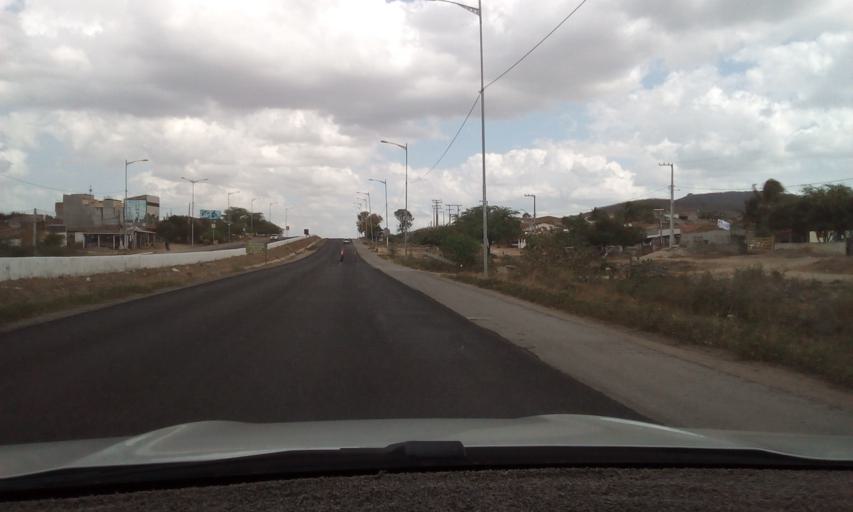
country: BR
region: Pernambuco
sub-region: Toritama
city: Toritama
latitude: -8.0795
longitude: -36.0441
